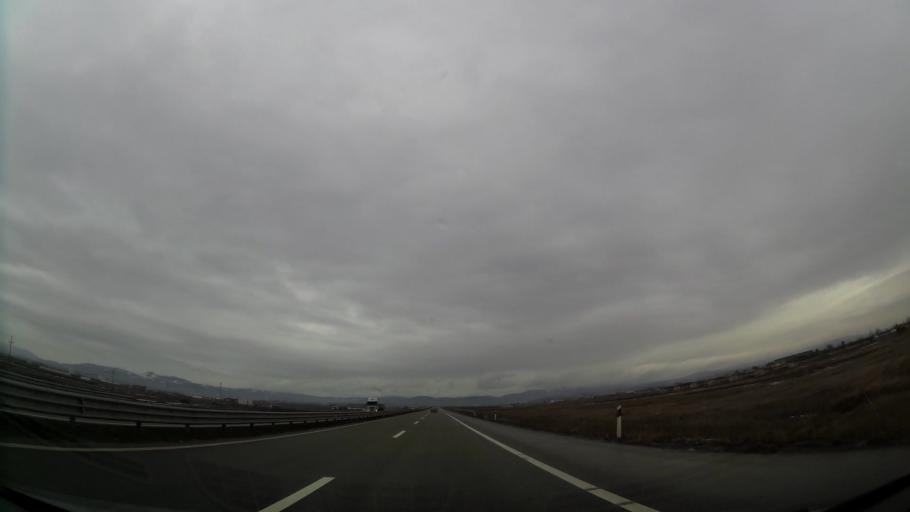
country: XK
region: Pristina
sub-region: Lipjan
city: Lipljan
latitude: 42.5306
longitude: 21.1487
